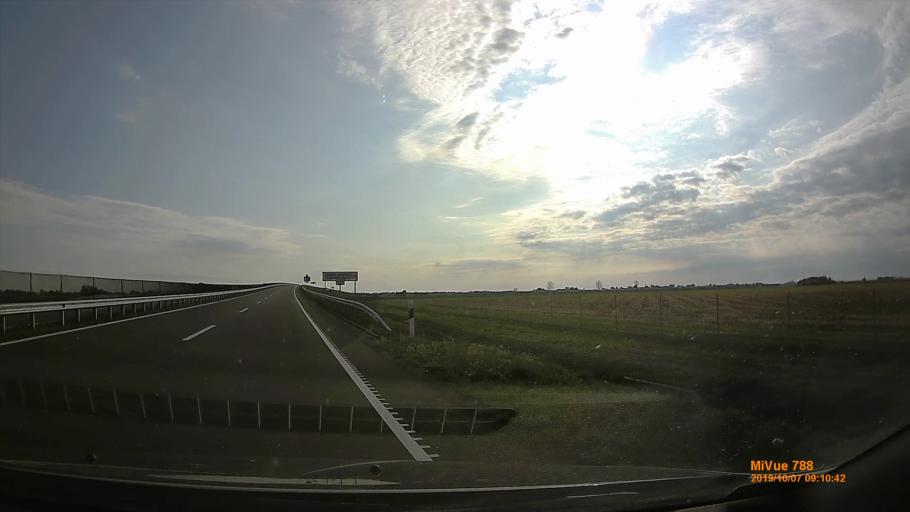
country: HU
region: Bekes
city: Szarvas
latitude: 46.8132
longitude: 20.6631
